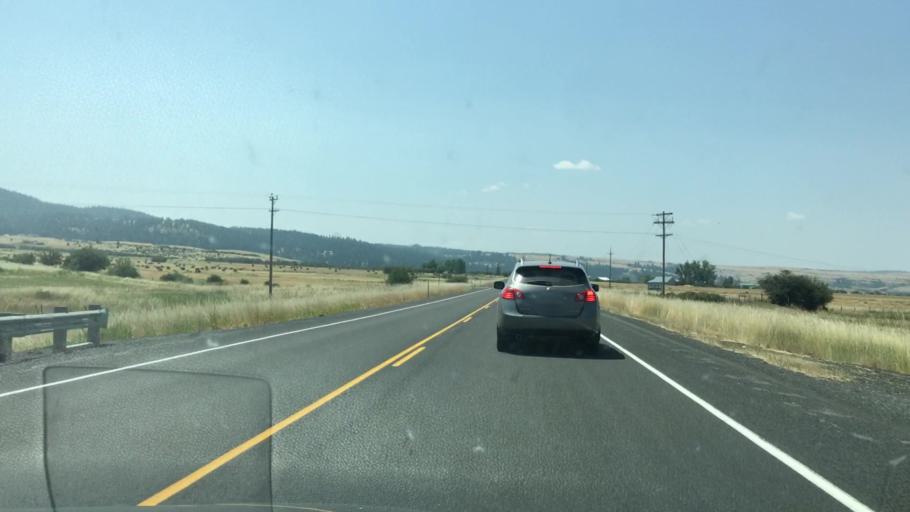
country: US
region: Idaho
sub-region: Idaho County
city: Grangeville
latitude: 45.9040
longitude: -116.1753
